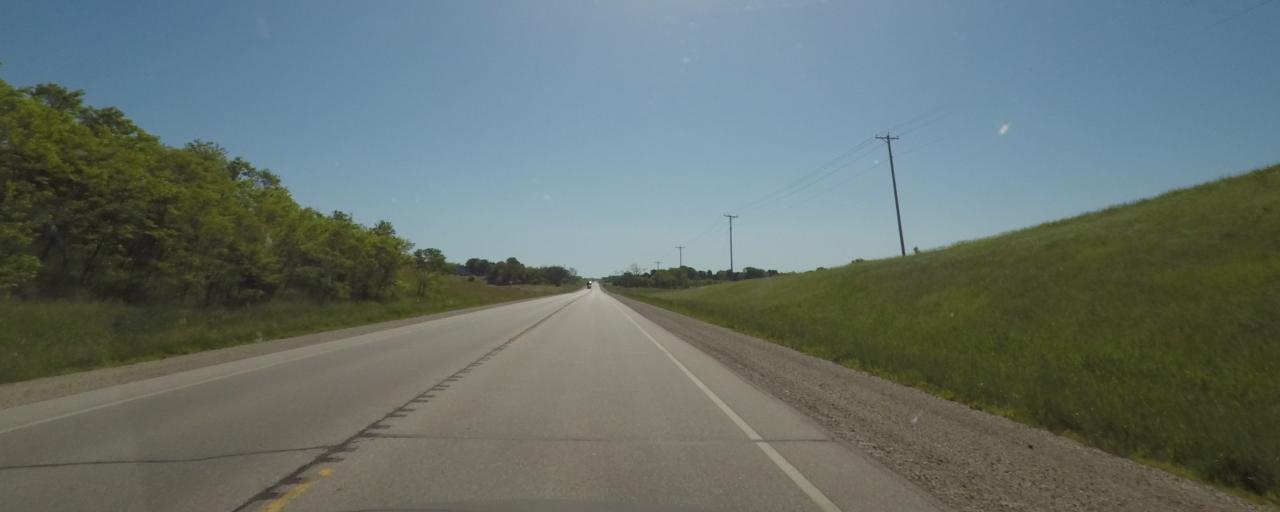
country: US
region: Wisconsin
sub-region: Fond du Lac County
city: Saint Peter
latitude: 43.7834
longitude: -88.3397
